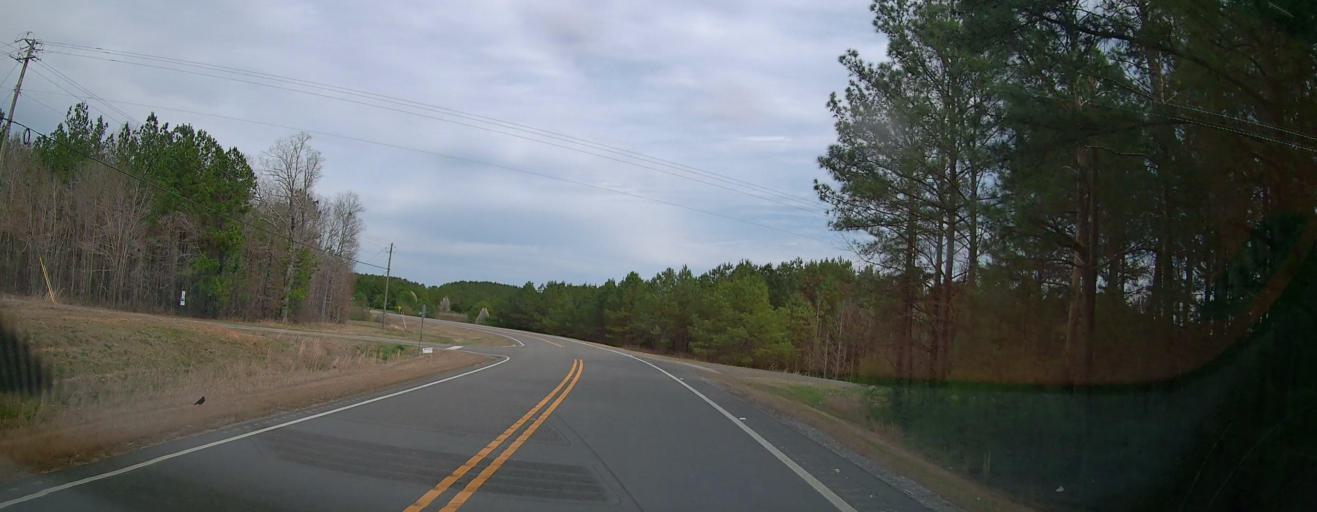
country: US
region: Alabama
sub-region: Walker County
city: Carbon Hill
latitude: 33.8662
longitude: -87.4194
